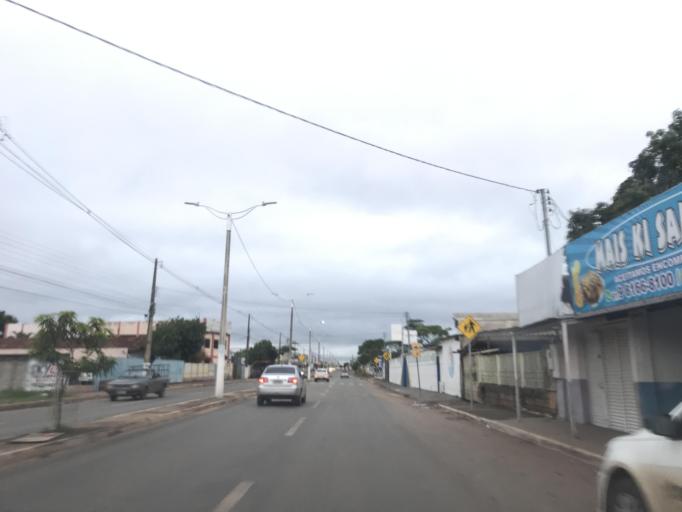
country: BR
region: Goias
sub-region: Luziania
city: Luziania
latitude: -16.2080
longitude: -47.9266
